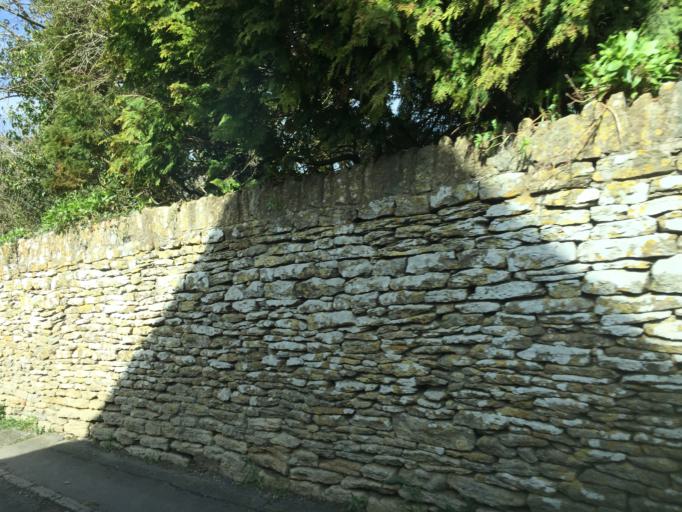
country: GB
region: England
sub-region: Wiltshire
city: Chippenham
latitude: 51.4993
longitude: -2.1454
